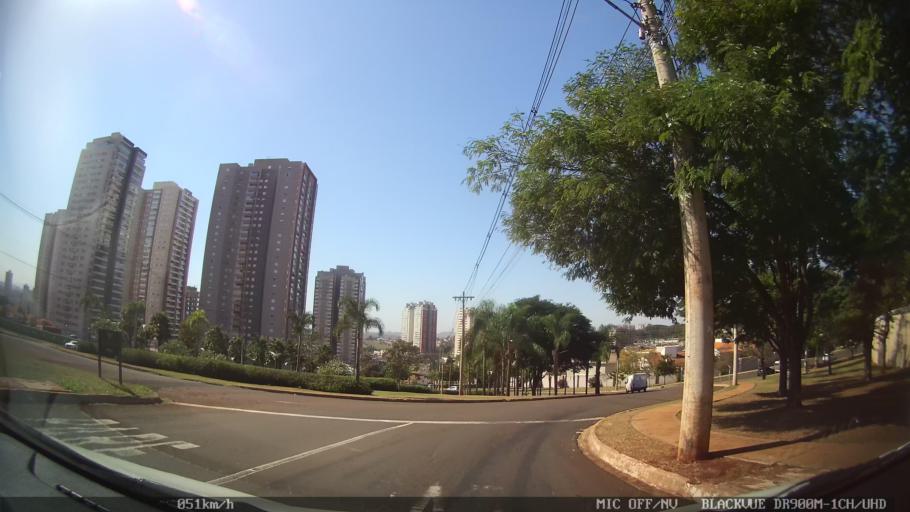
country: BR
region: Sao Paulo
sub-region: Ribeirao Preto
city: Ribeirao Preto
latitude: -21.2195
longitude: -47.8016
